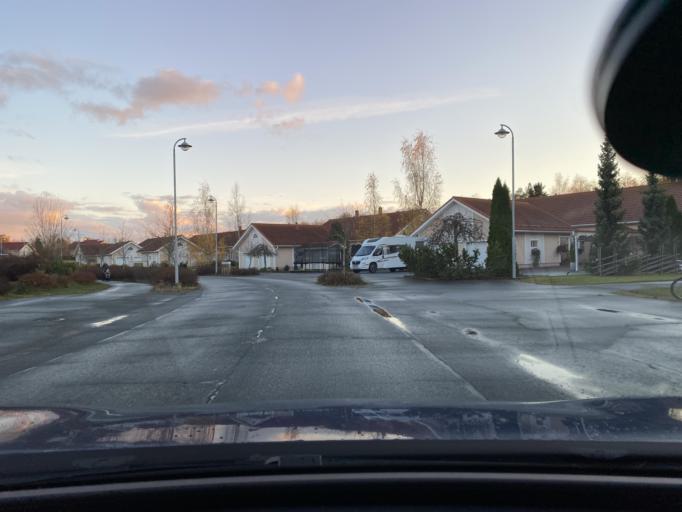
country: FI
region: Satakunta
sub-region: Pori
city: Huittinen
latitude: 61.1816
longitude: 22.7037
